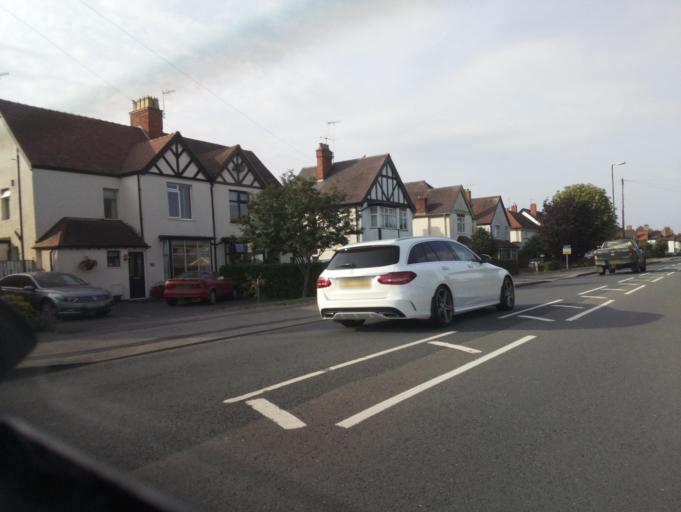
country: GB
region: England
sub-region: Worcestershire
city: Evesham
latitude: 52.0777
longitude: -1.9527
